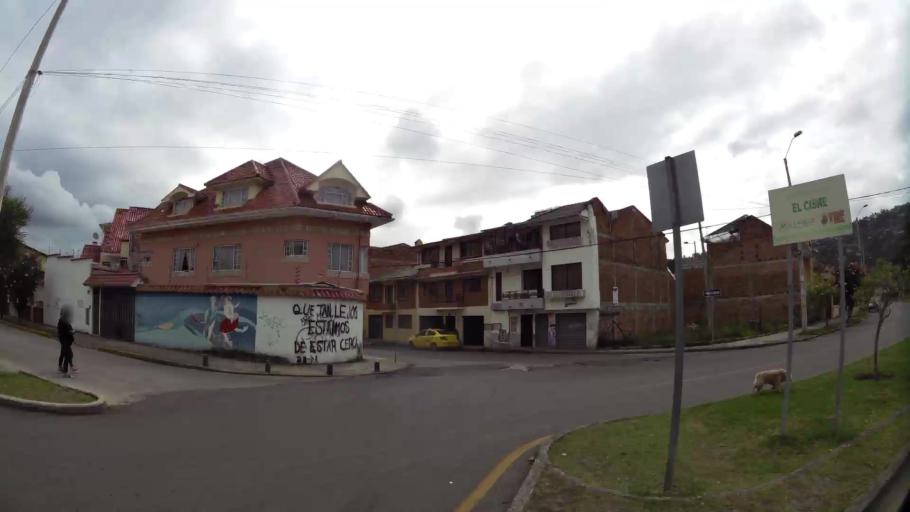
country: EC
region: Azuay
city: Cuenca
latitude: -2.9018
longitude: -78.9824
